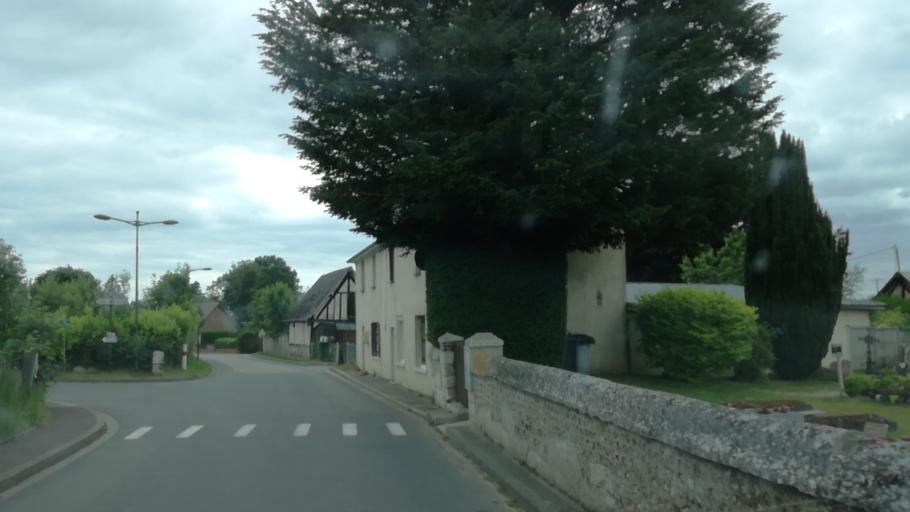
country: FR
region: Haute-Normandie
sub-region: Departement de l'Eure
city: Bourg-Achard
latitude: 49.3227
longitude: 0.8080
